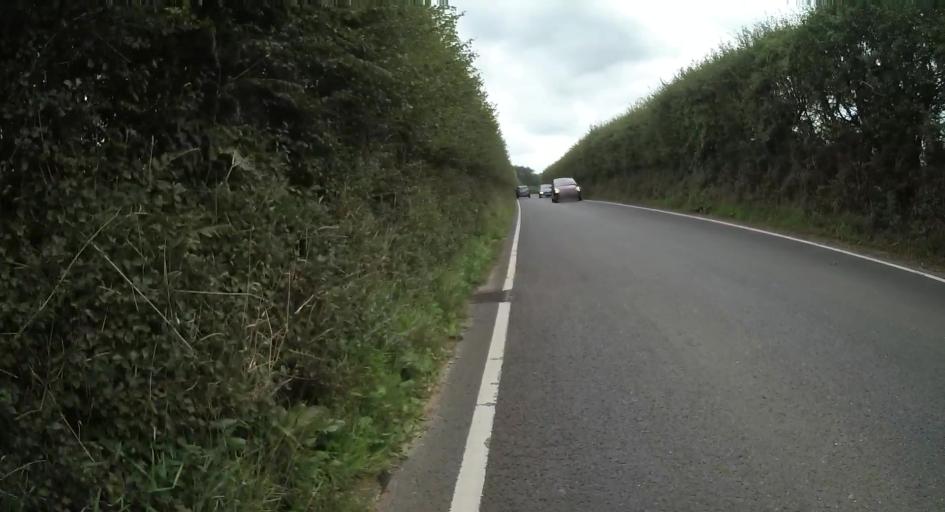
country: GB
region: England
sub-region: Isle of Wight
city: Niton
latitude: 50.6204
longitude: -1.2654
